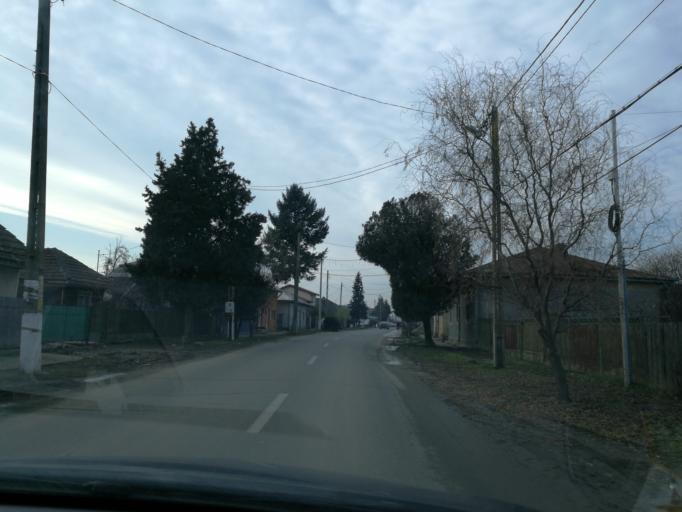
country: RO
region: Ialomita
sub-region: Comuna Fierbinti-Targ
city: Fierbintii de Jos
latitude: 44.6842
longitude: 26.3854
